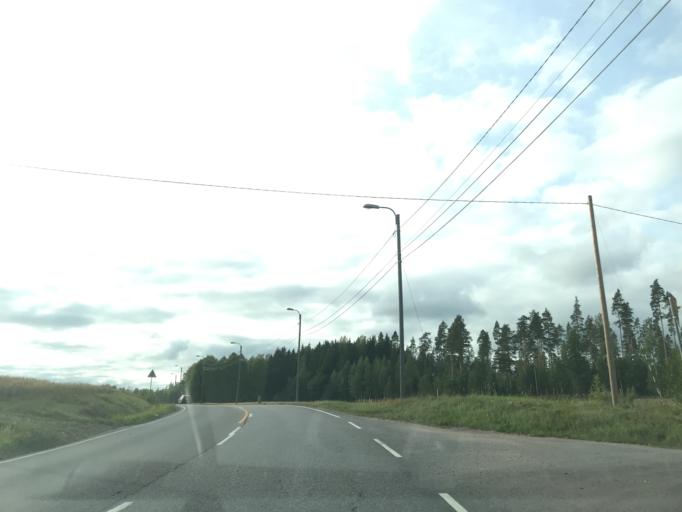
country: FI
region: Uusimaa
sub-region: Helsinki
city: Kirkkonummi
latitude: 60.2048
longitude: 24.5000
